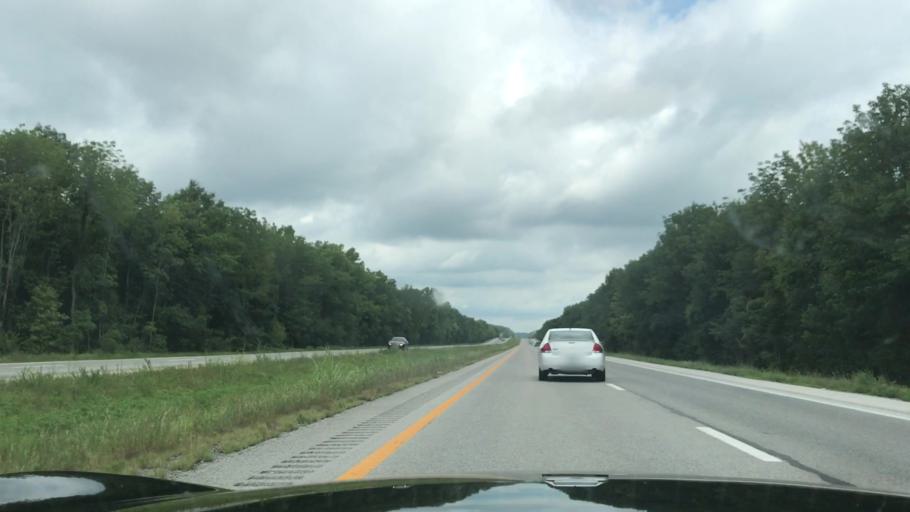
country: US
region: Kentucky
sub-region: Butler County
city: Morgantown
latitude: 37.1285
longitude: -86.6457
